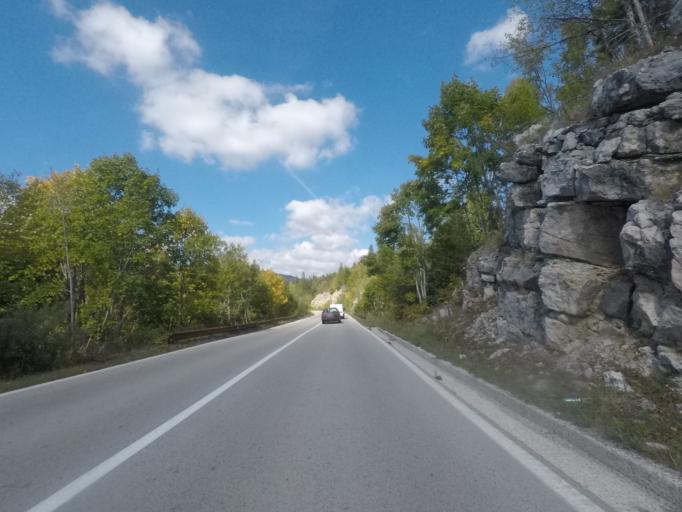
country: ME
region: Opstina Niksic
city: Niksic
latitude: 42.9411
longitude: 18.9161
